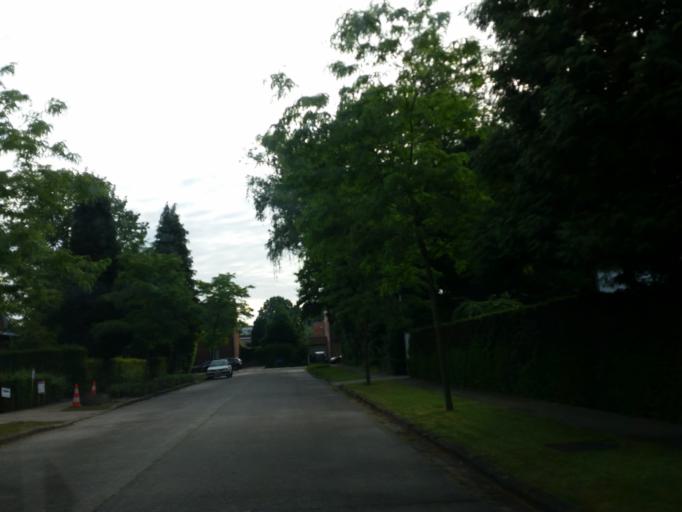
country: BE
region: Flanders
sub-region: Provincie Antwerpen
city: Kapellen
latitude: 51.3063
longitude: 4.4514
